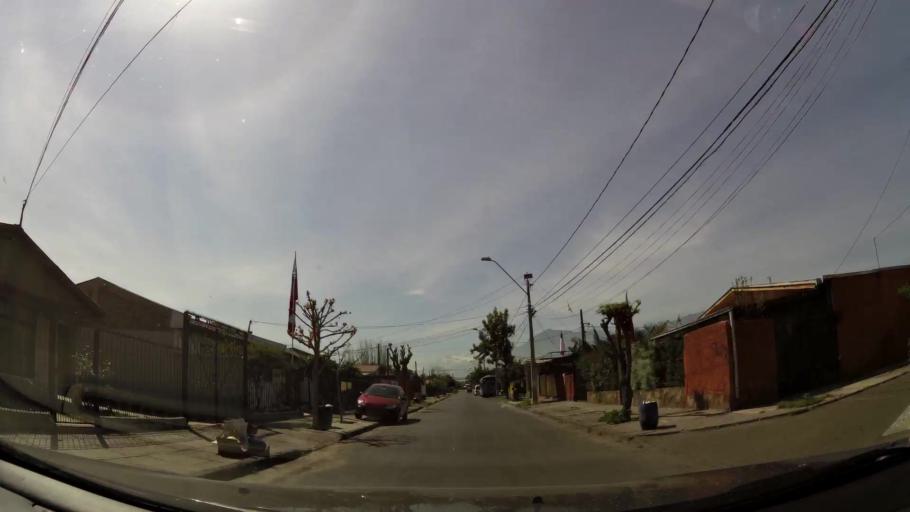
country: CL
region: Santiago Metropolitan
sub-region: Provincia de Cordillera
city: Puente Alto
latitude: -33.6182
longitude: -70.5766
